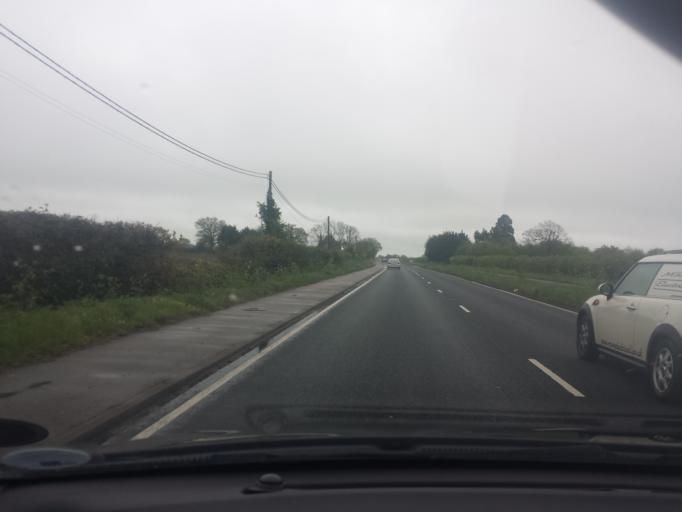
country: GB
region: England
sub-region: Essex
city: Wivenhoe
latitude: 51.8815
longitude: 0.9614
